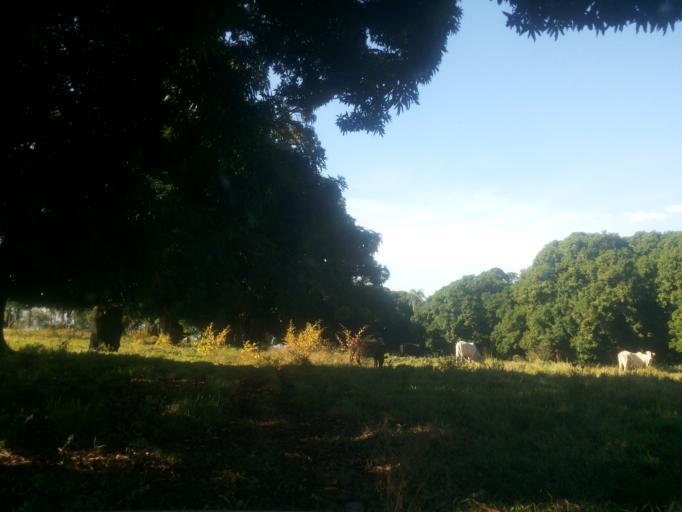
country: BR
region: Minas Gerais
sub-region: Santa Vitoria
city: Santa Vitoria
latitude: -18.9981
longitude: -50.4484
